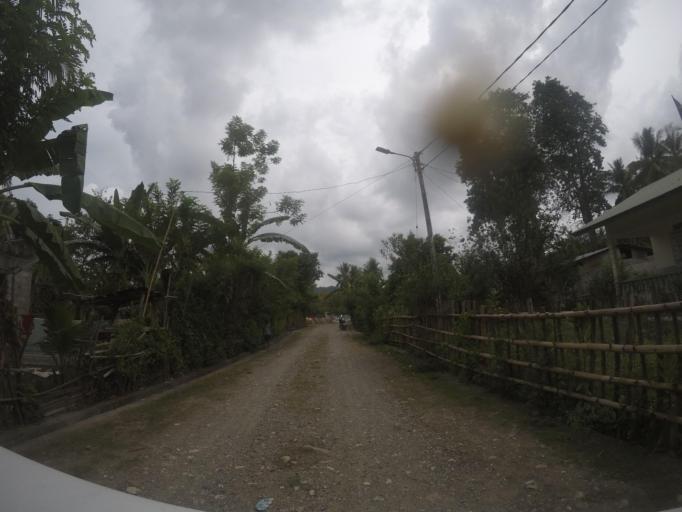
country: TL
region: Viqueque
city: Viqueque
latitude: -8.8762
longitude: 126.3677
